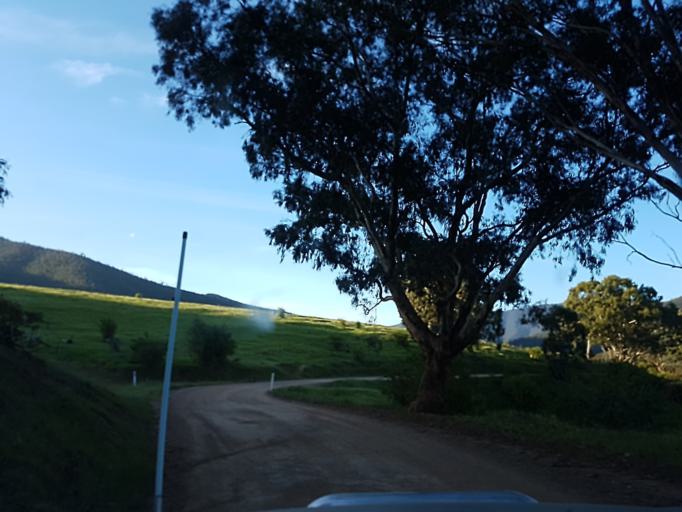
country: AU
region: Victoria
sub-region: East Gippsland
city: Bairnsdale
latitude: -37.4035
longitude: 147.1033
